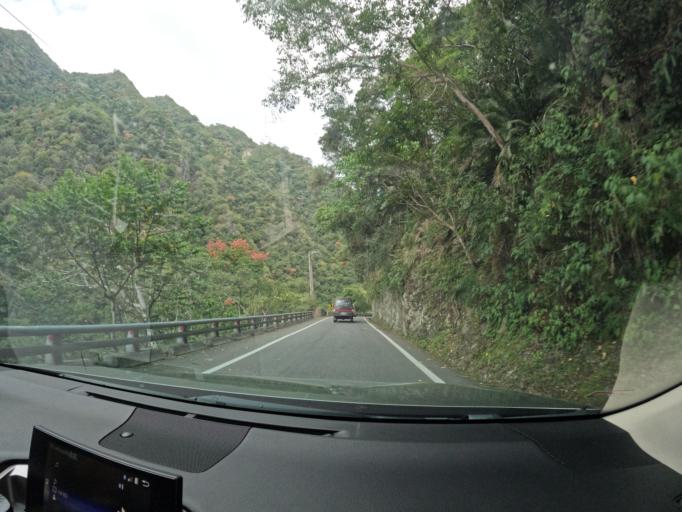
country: TW
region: Taiwan
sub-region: Taitung
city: Taitung
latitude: 23.1415
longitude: 121.1005
